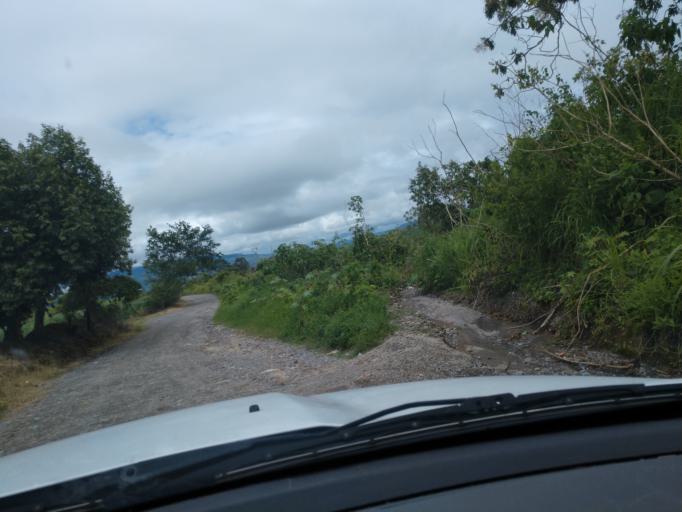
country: MX
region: Nayarit
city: Xalisco
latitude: 21.4360
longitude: -104.9249
